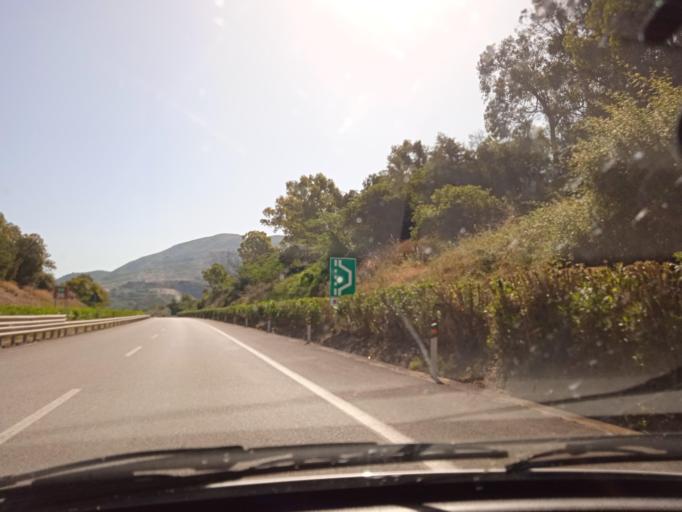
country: IT
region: Sicily
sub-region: Messina
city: Torrenova
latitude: 38.0815
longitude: 14.6789
